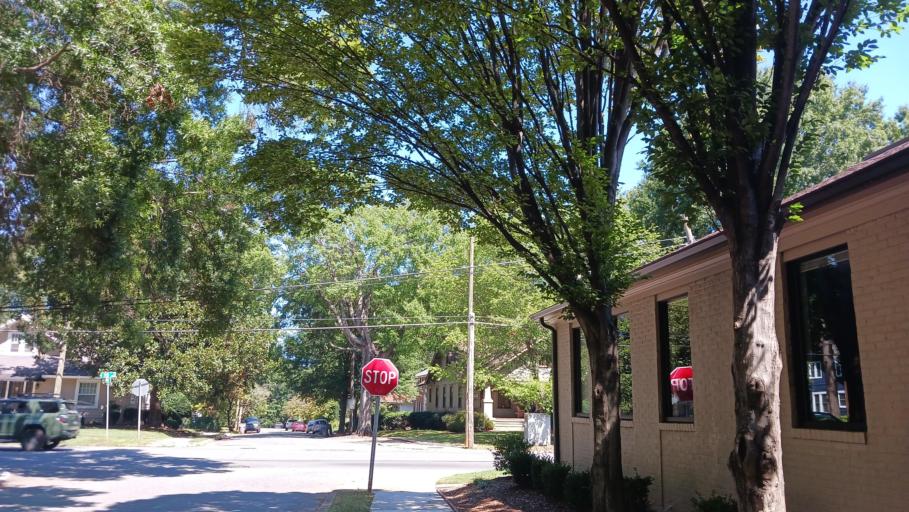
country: US
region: North Carolina
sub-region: Mecklenburg County
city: Charlotte
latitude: 35.2104
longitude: -80.8159
